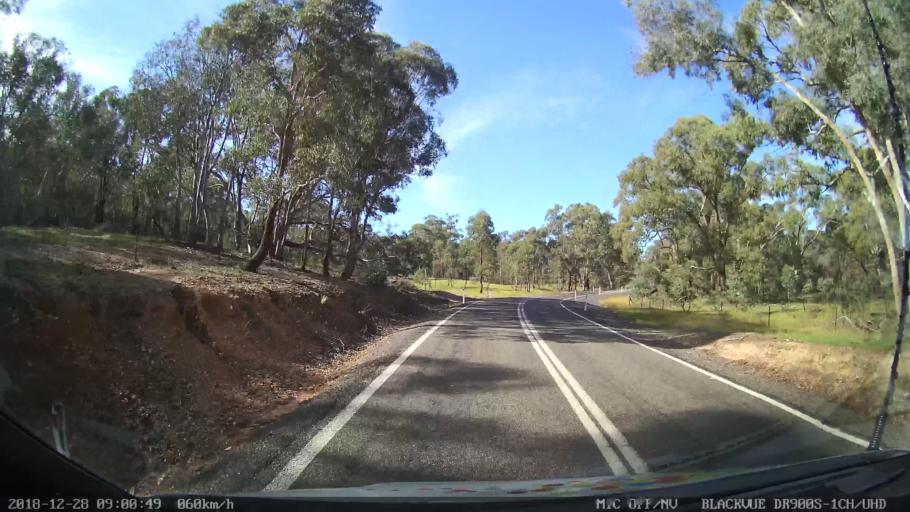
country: AU
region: New South Wales
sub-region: Upper Lachlan Shire
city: Crookwell
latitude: -34.1418
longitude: 149.3347
